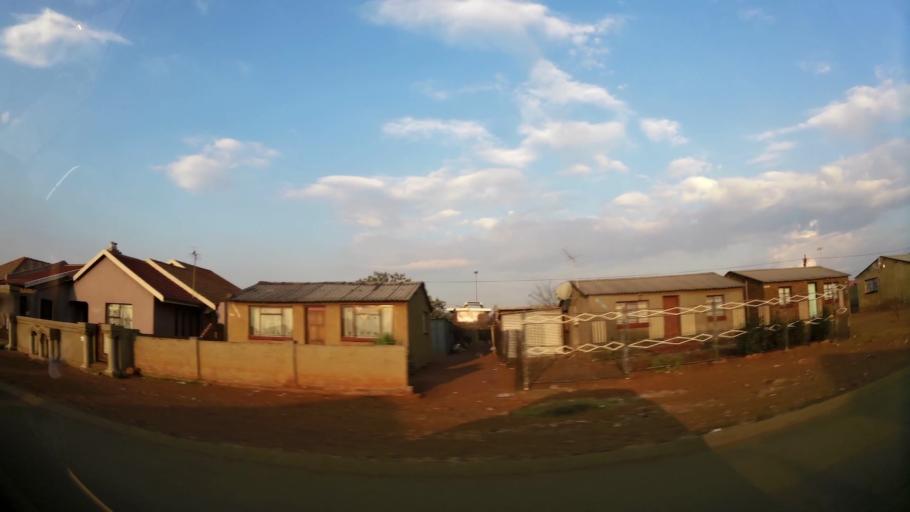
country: ZA
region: Gauteng
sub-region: City of Johannesburg Metropolitan Municipality
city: Orange Farm
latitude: -26.5546
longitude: 27.8630
